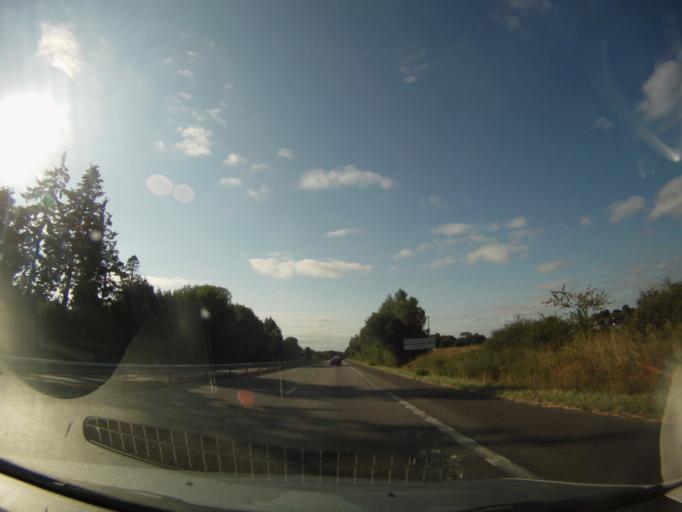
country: FR
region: Pays de la Loire
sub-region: Departement de la Loire-Atlantique
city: Treillieres
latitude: 47.3102
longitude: -1.6391
